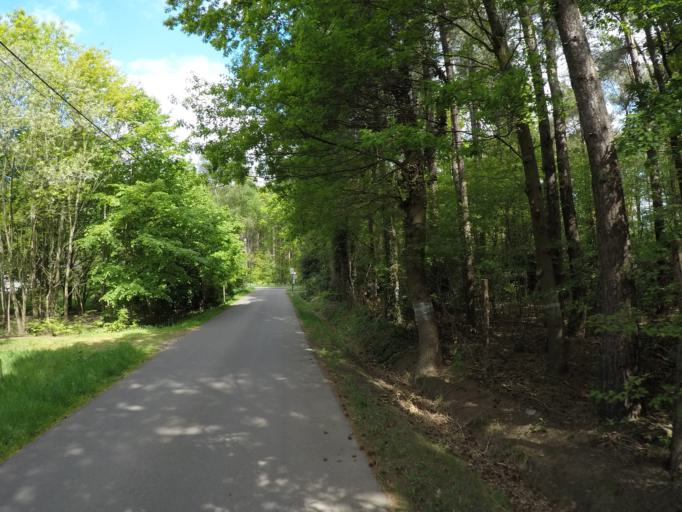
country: BE
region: Flanders
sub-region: Provincie Antwerpen
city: Herenthout
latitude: 51.1329
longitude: 4.7192
